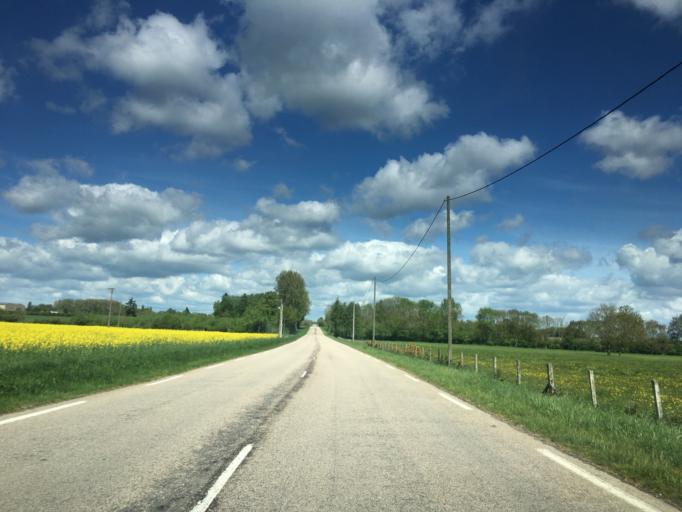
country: FR
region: Lower Normandy
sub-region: Departement de l'Orne
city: Rai
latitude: 48.8131
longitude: 0.5770
